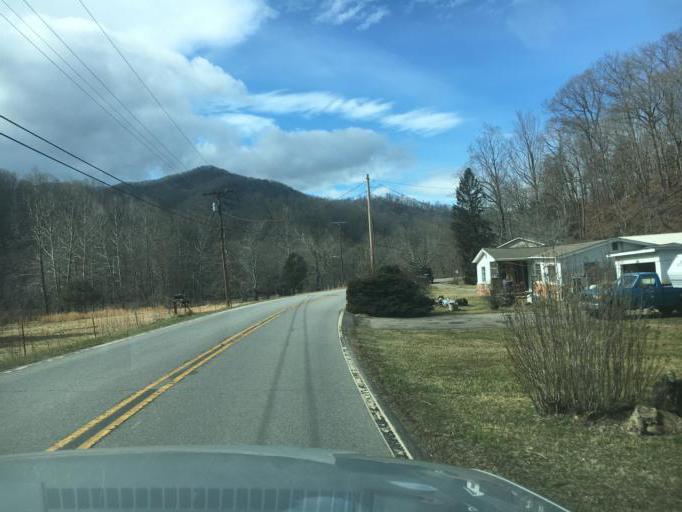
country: US
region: North Carolina
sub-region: Haywood County
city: Canton
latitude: 35.4497
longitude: -82.8277
